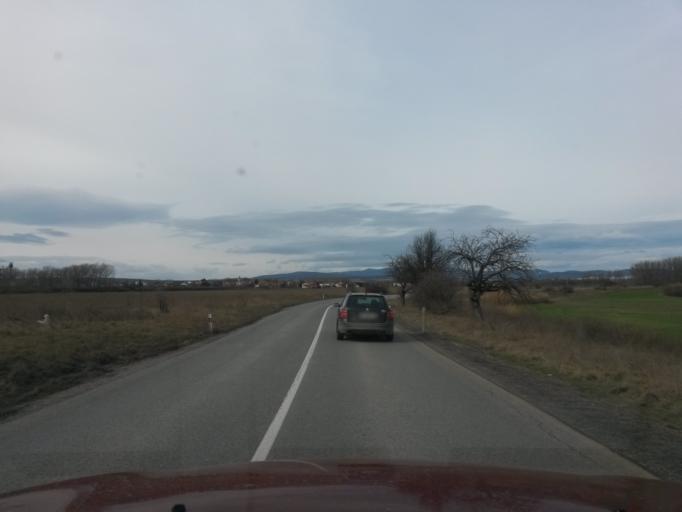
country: SK
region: Kosicky
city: Kosice
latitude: 48.6517
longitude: 21.2842
